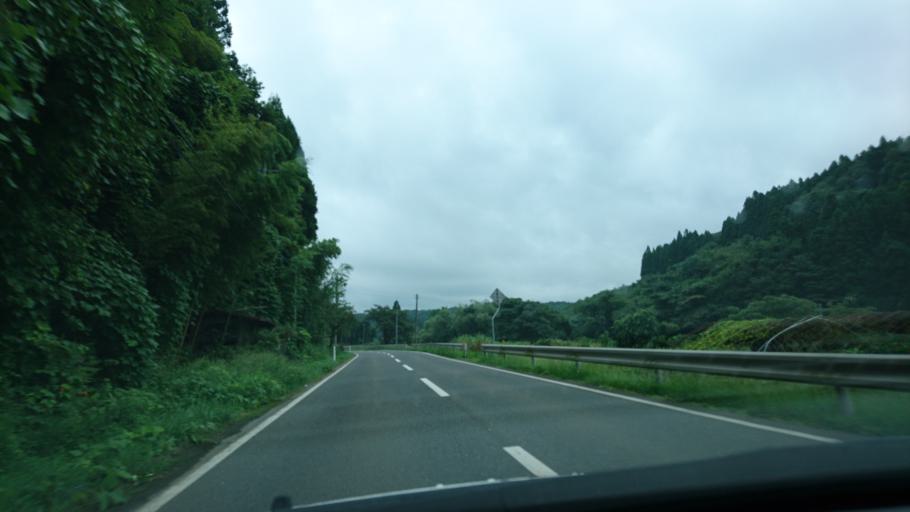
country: JP
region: Iwate
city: Ichinoseki
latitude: 38.9107
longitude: 141.0560
